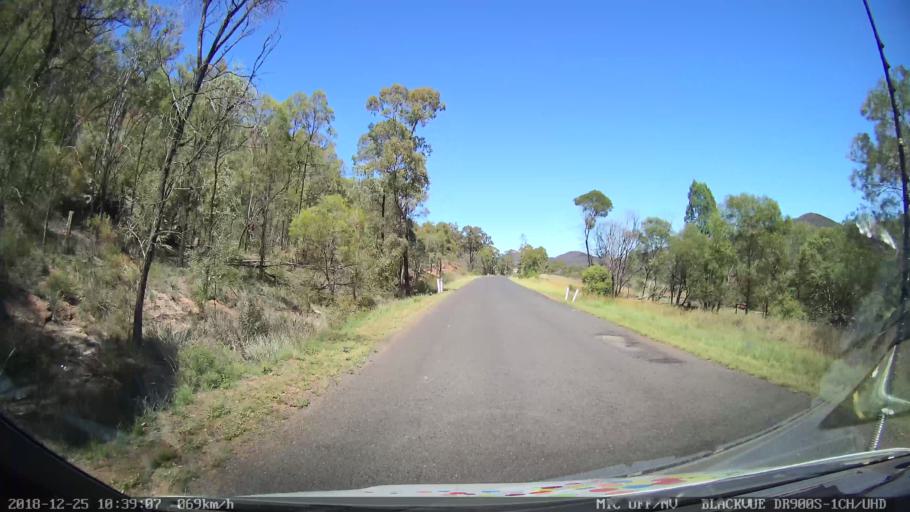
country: AU
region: New South Wales
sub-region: Upper Hunter Shire
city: Merriwa
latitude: -32.4045
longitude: 150.3605
